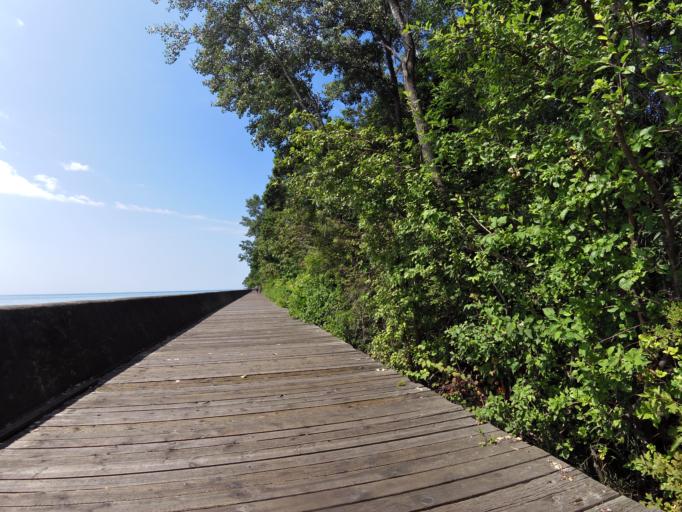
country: CA
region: Ontario
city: Toronto
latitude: 43.6248
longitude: -79.3589
